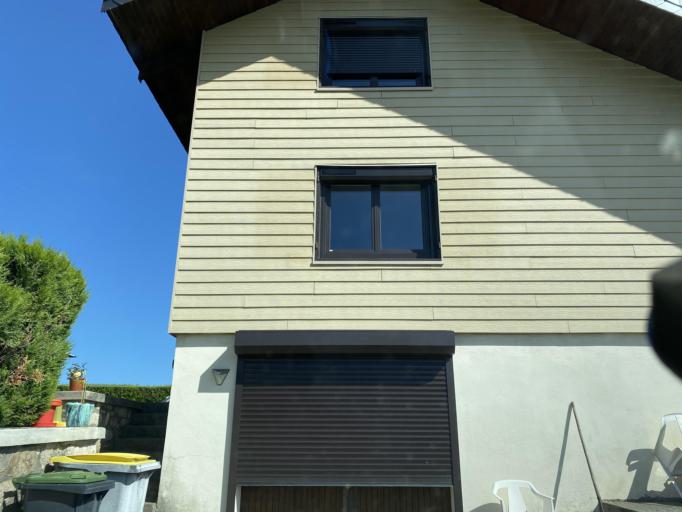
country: FR
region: Auvergne
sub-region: Departement du Puy-de-Dome
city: Celles-sur-Durolle
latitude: 45.7743
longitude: 3.6718
